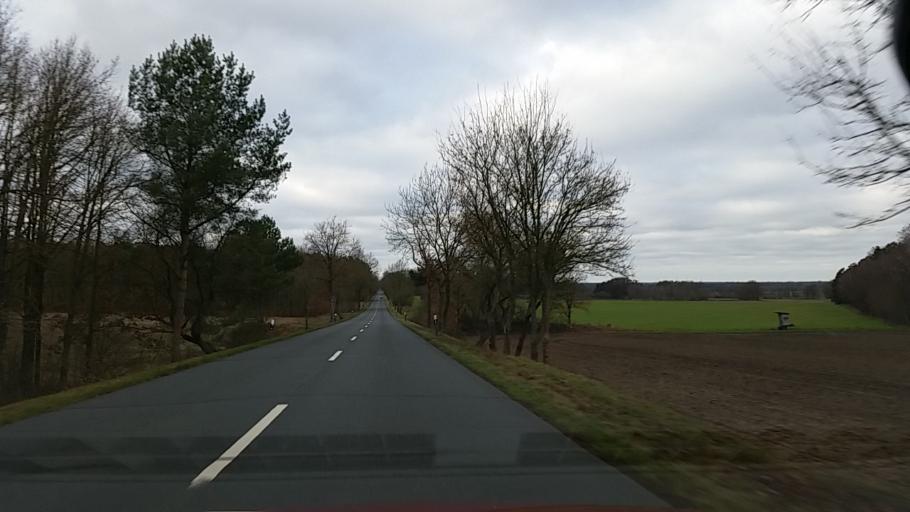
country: DE
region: Lower Saxony
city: Wrestedt
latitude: 52.8829
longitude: 10.6110
